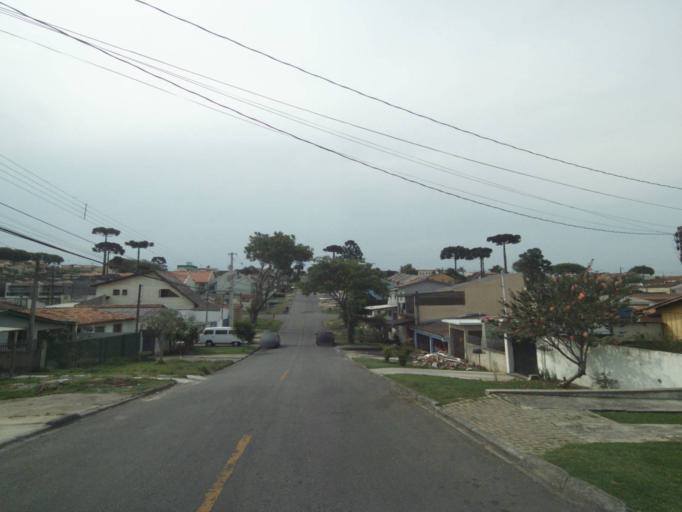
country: BR
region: Parana
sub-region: Pinhais
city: Pinhais
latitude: -25.3970
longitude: -49.2006
